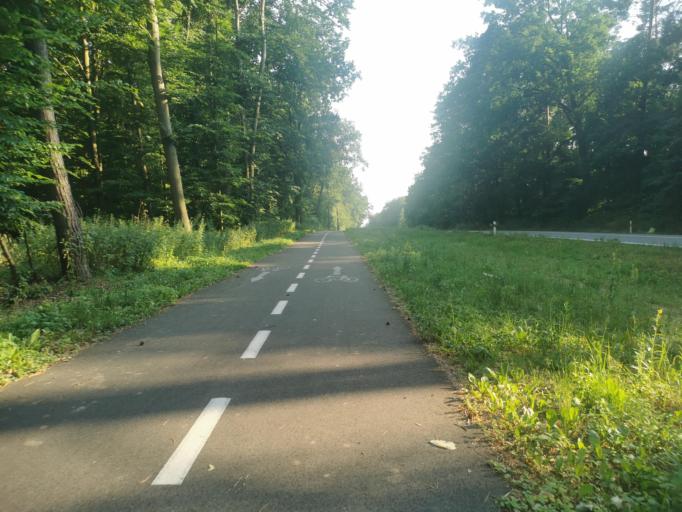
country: CZ
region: South Moravian
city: Ratiskovice
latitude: 48.9022
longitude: 17.1588
